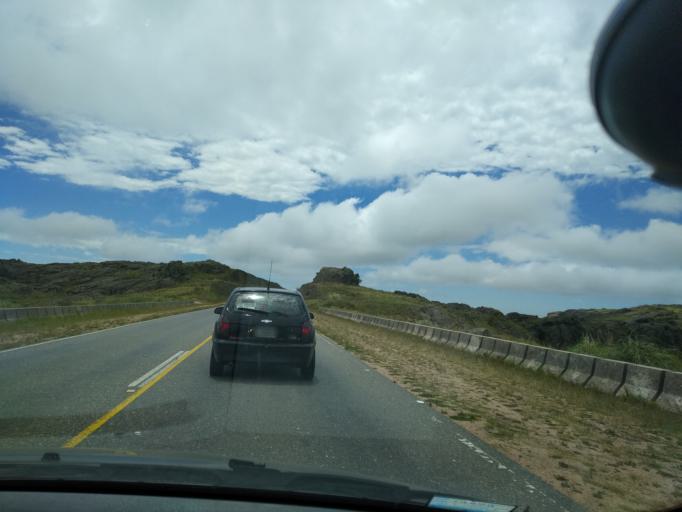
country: AR
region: Cordoba
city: Cuesta Blanca
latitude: -31.6081
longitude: -64.7317
